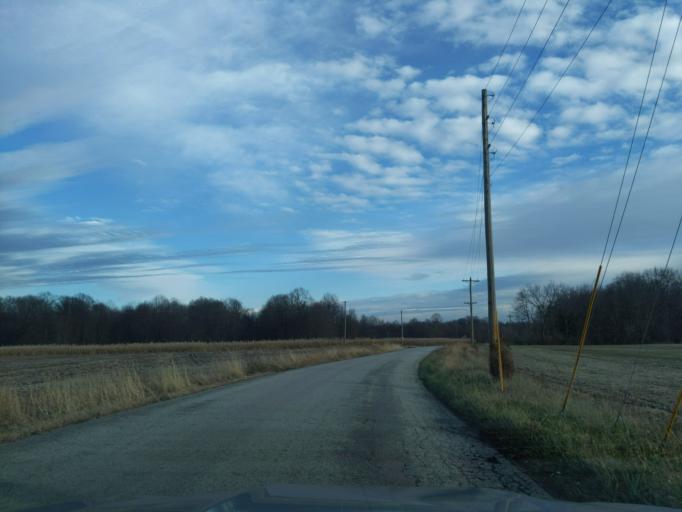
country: US
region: Indiana
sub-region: Decatur County
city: Greensburg
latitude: 39.2148
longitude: -85.4502
